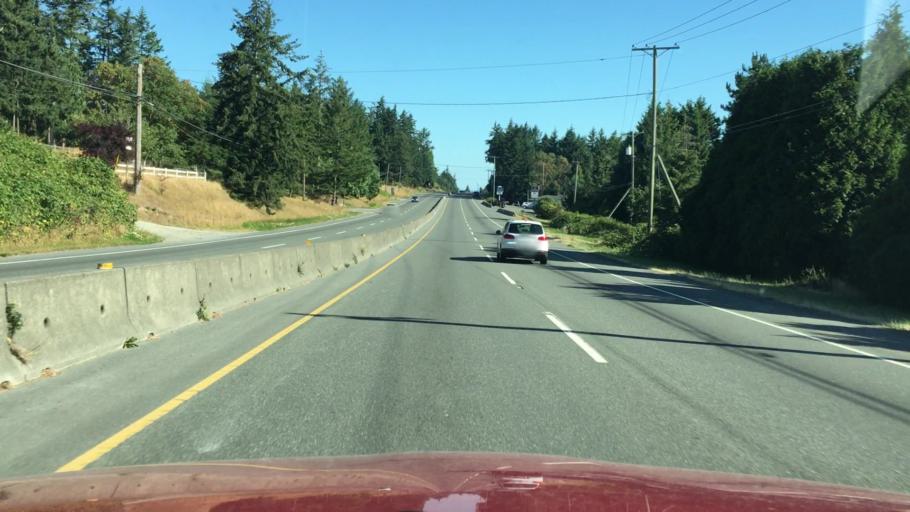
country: CA
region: British Columbia
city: Victoria
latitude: 48.5471
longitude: -123.3914
